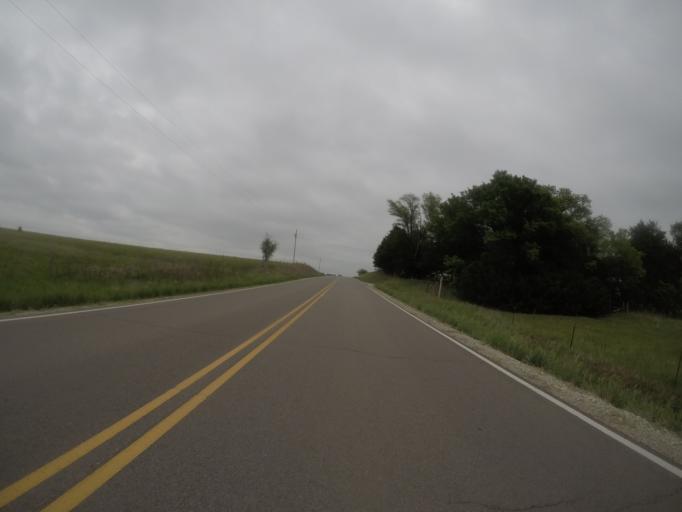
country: US
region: Kansas
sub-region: Pottawatomie County
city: Westmoreland
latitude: 39.5078
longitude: -96.1942
